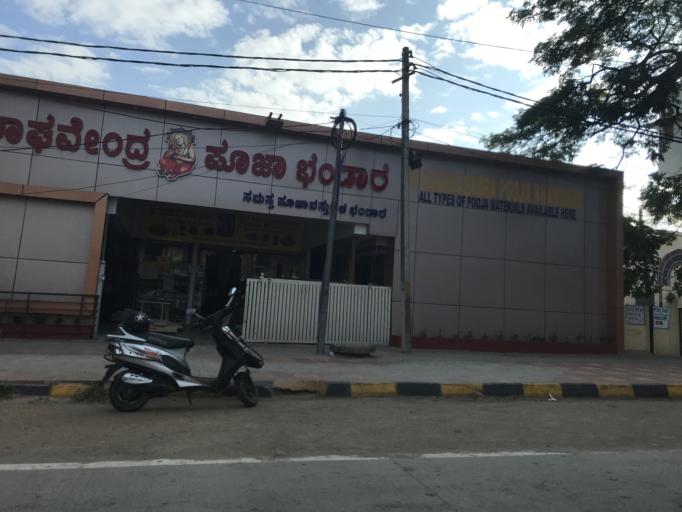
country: IN
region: Karnataka
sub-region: Mysore
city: Mysore
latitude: 12.3019
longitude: 76.6489
